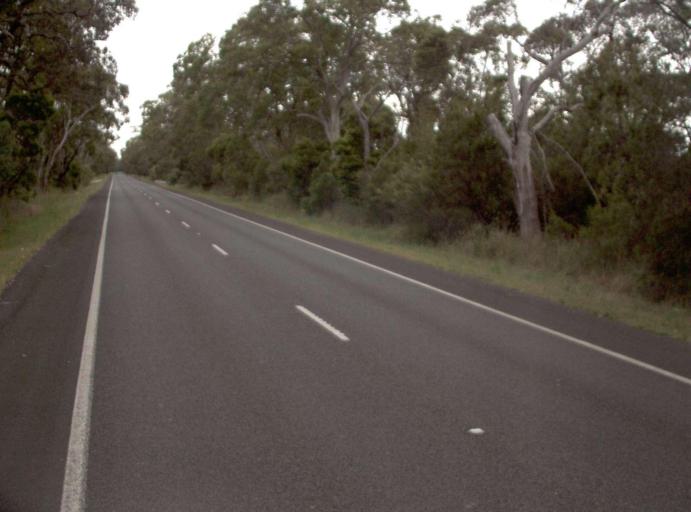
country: AU
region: Victoria
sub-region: Latrobe
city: Traralgon
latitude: -38.5498
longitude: 146.8238
